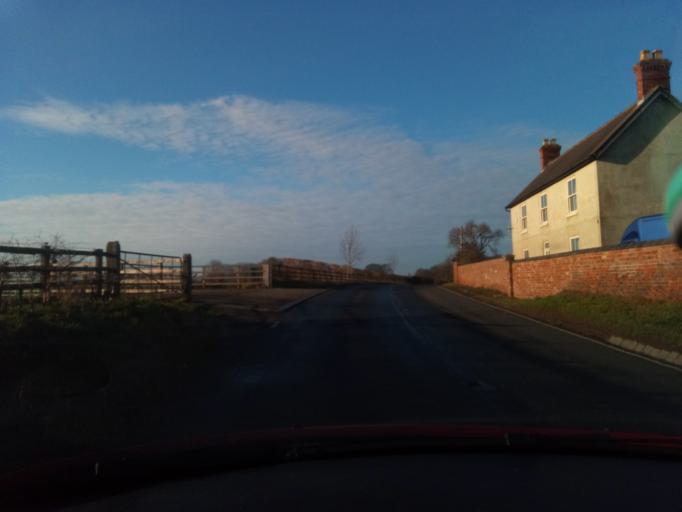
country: GB
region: England
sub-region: North Yorkshire
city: Thirsk
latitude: 54.2125
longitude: -1.4467
